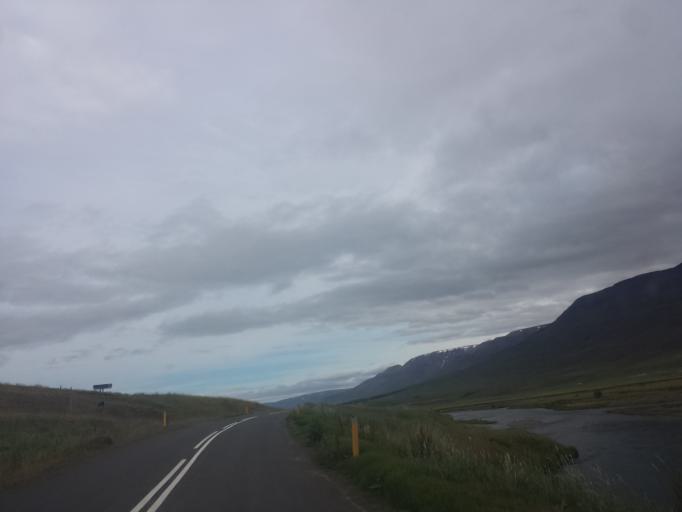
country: IS
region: Northeast
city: Akureyri
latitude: 65.4474
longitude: -18.2075
